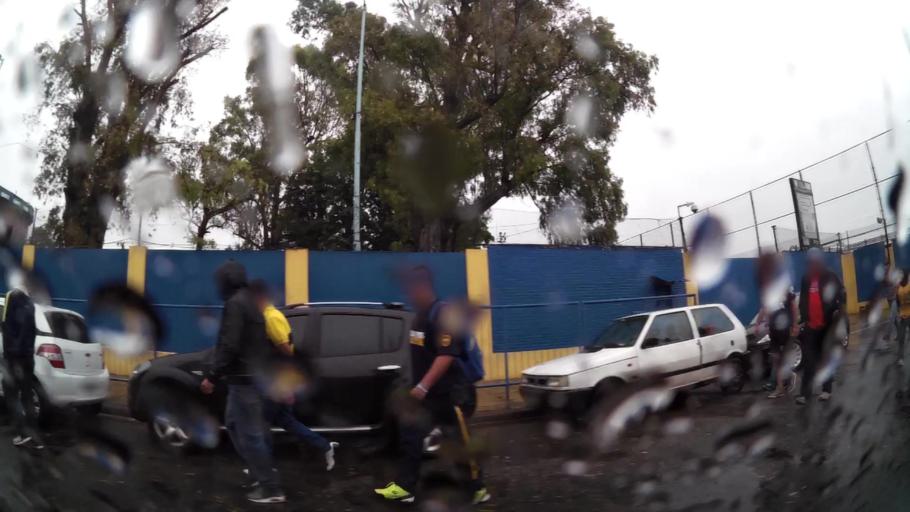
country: AR
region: Buenos Aires F.D.
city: Buenos Aires
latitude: -34.6338
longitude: -58.3652
